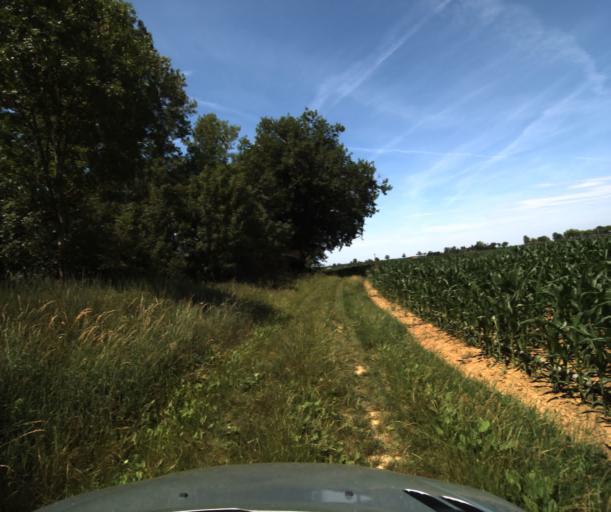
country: FR
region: Midi-Pyrenees
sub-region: Departement de la Haute-Garonne
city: Labastidette
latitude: 43.4624
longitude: 1.2246
